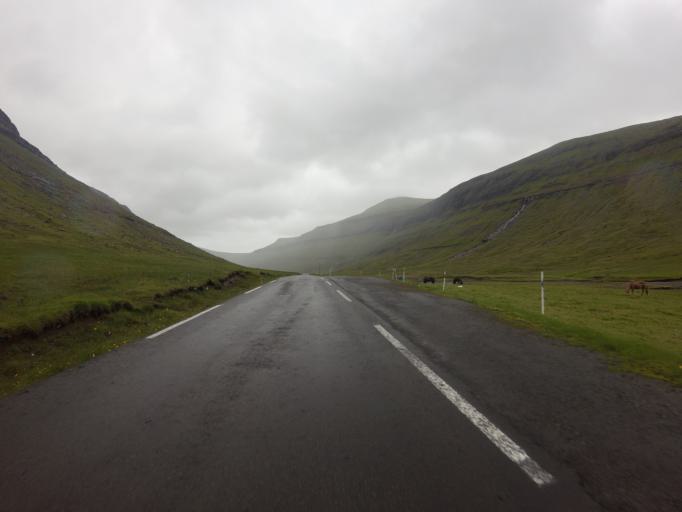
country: FO
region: Streymoy
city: Vestmanna
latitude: 62.2314
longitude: -7.1382
